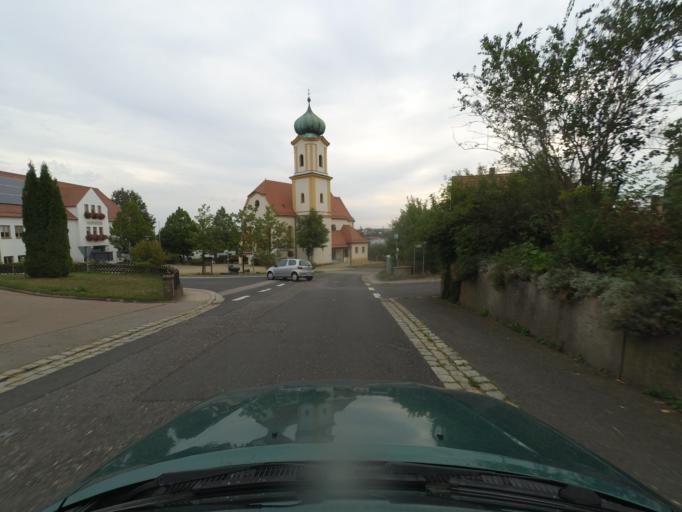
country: DE
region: Bavaria
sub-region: Upper Palatinate
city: Edelsfeld
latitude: 49.5767
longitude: 11.6931
